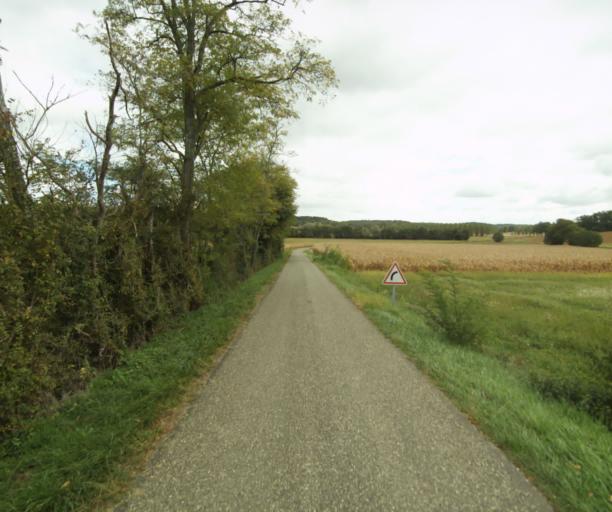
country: FR
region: Midi-Pyrenees
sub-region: Departement du Gers
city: Nogaro
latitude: 43.8459
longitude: -0.0091
